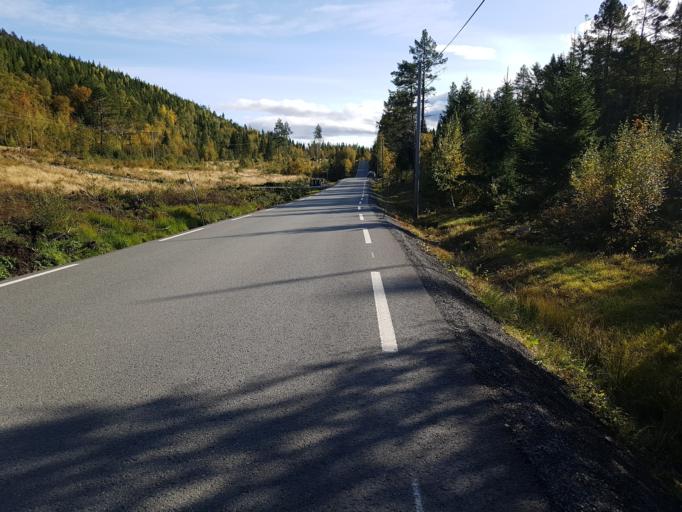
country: NO
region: Sor-Trondelag
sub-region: Malvik
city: Malvik
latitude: 63.3728
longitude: 10.6128
